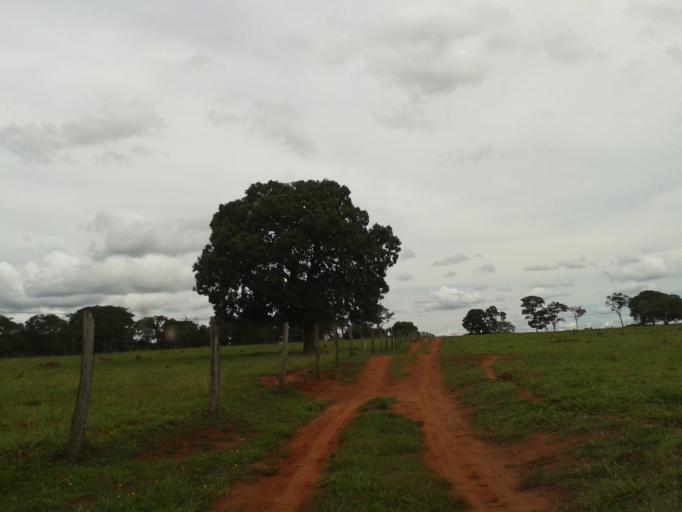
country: BR
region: Minas Gerais
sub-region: Santa Vitoria
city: Santa Vitoria
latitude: -18.7894
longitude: -49.8560
